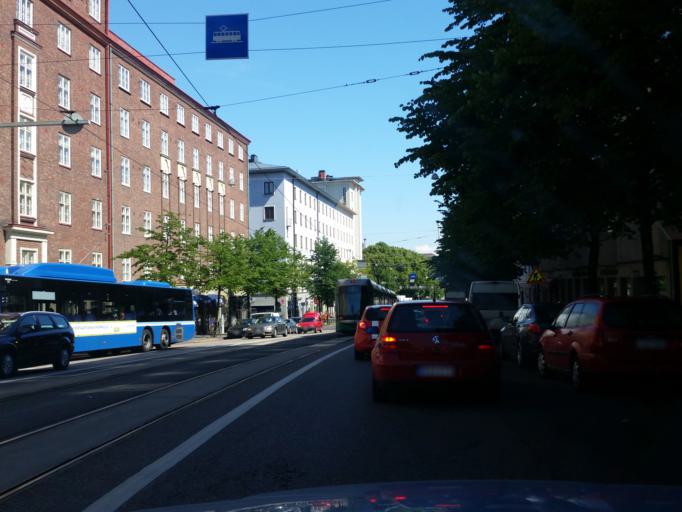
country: FI
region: Uusimaa
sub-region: Helsinki
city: Helsinki
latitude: 60.1806
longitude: 24.9247
